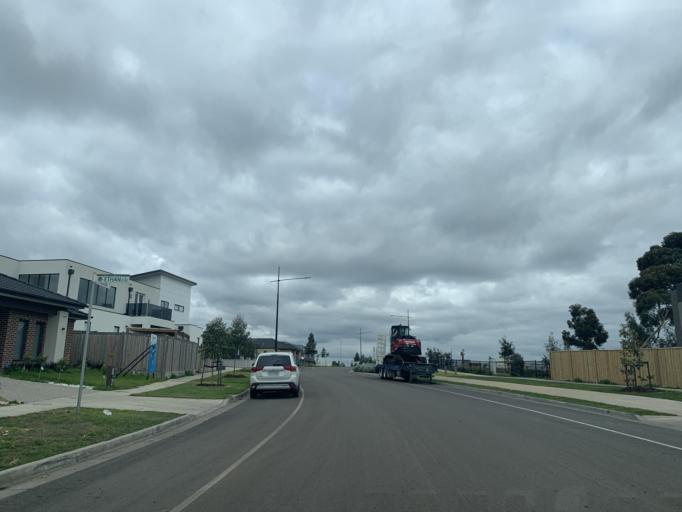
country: AU
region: Victoria
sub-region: Hume
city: Craigieburn
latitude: -37.5978
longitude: 144.9877
